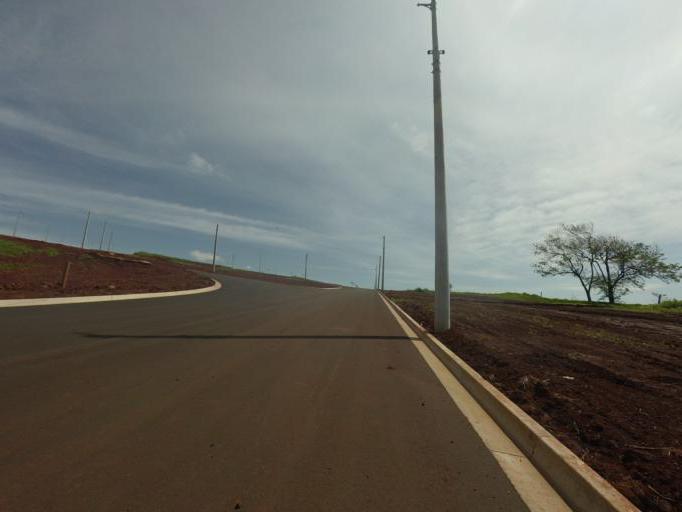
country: BR
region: Sao Paulo
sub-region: Piracicaba
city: Piracicaba
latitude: -22.7628
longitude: -47.5796
